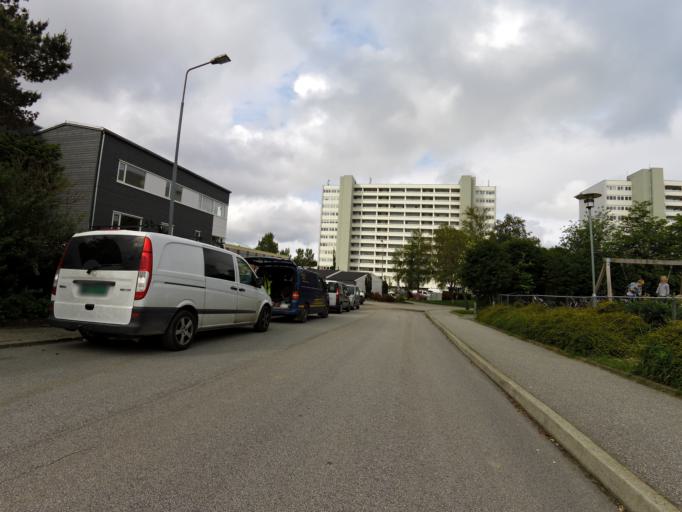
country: NO
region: Rogaland
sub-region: Stavanger
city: Stavanger
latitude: 58.9571
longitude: 5.6951
